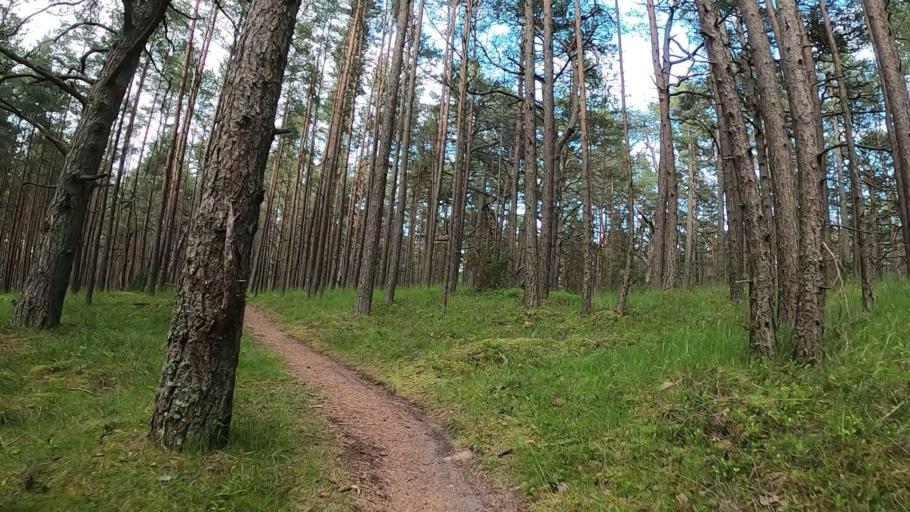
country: LV
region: Carnikava
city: Carnikava
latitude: 57.1169
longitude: 24.1993
